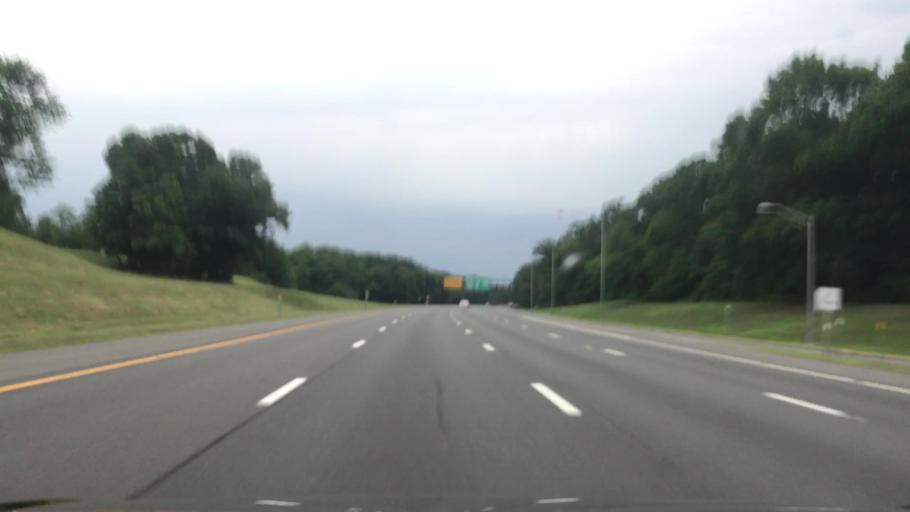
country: US
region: New Jersey
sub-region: Monmouth County
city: Shark River Hills
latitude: 40.2228
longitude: -74.0971
